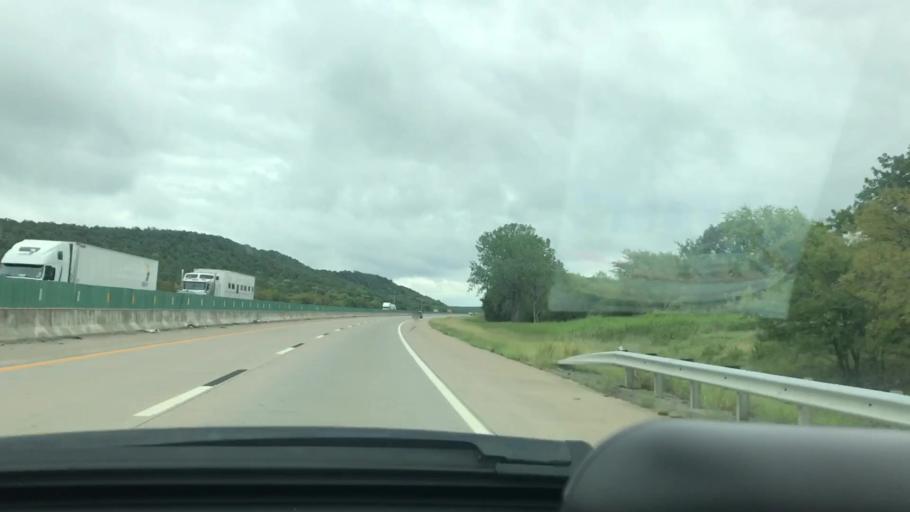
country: US
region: Oklahoma
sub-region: Pittsburg County
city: Krebs
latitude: 35.1106
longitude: -95.6921
